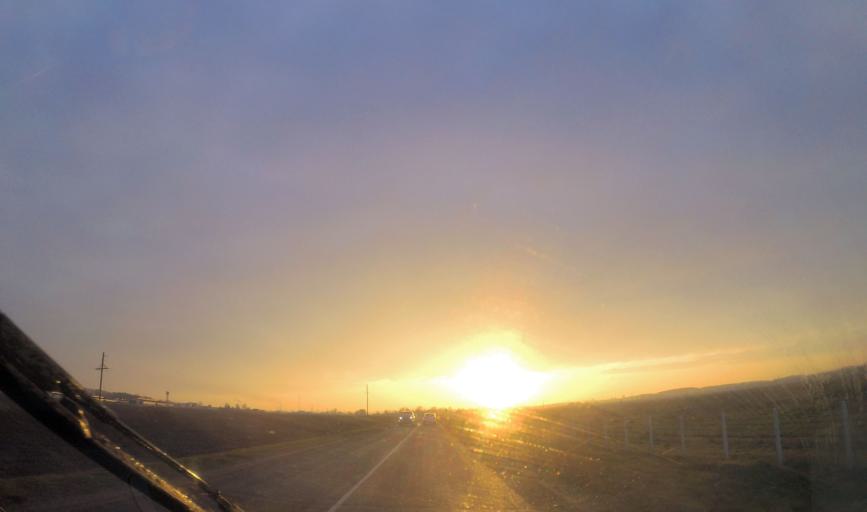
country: BY
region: Grodnenskaya
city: Hrodna
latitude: 53.7407
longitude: 23.9317
